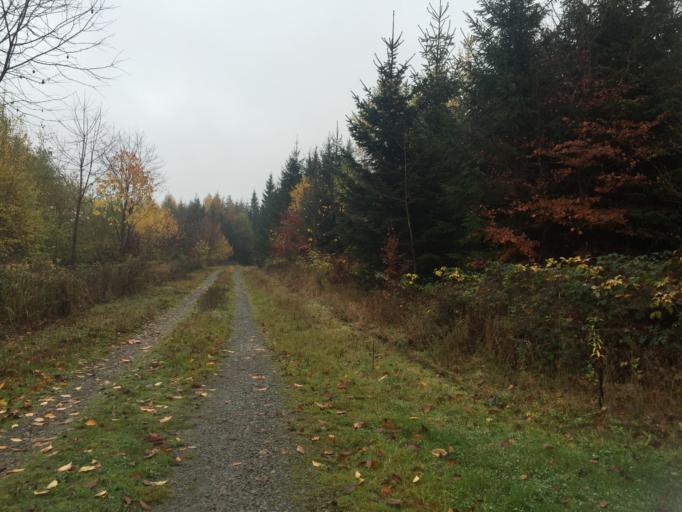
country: DE
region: Hesse
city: Hirschhorn
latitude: 49.4424
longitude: 8.8661
